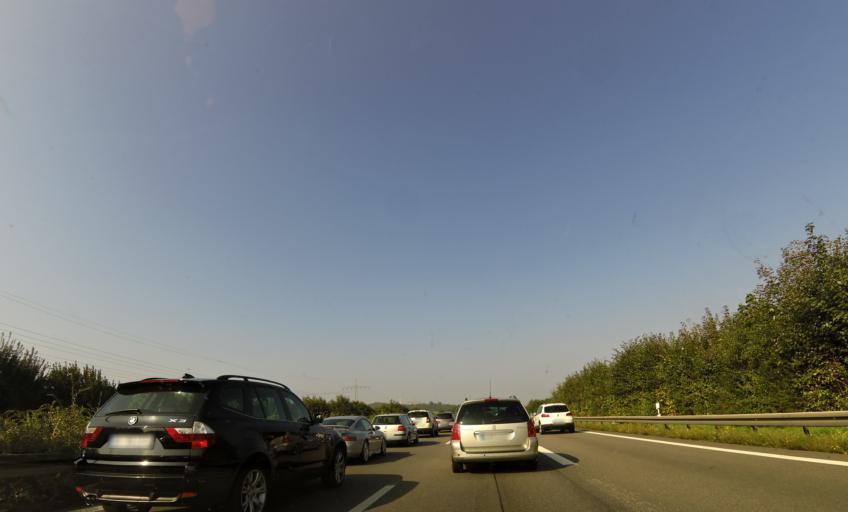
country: DE
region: Baden-Wuerttemberg
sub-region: Regierungsbezirk Stuttgart
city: Erlenbach
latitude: 49.1678
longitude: 9.2587
